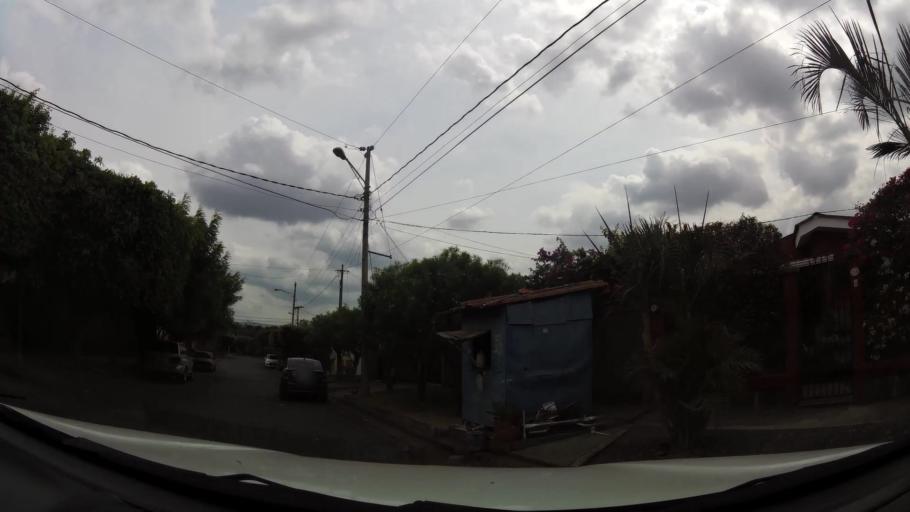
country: NI
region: Managua
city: Managua
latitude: 12.1105
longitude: -86.2459
